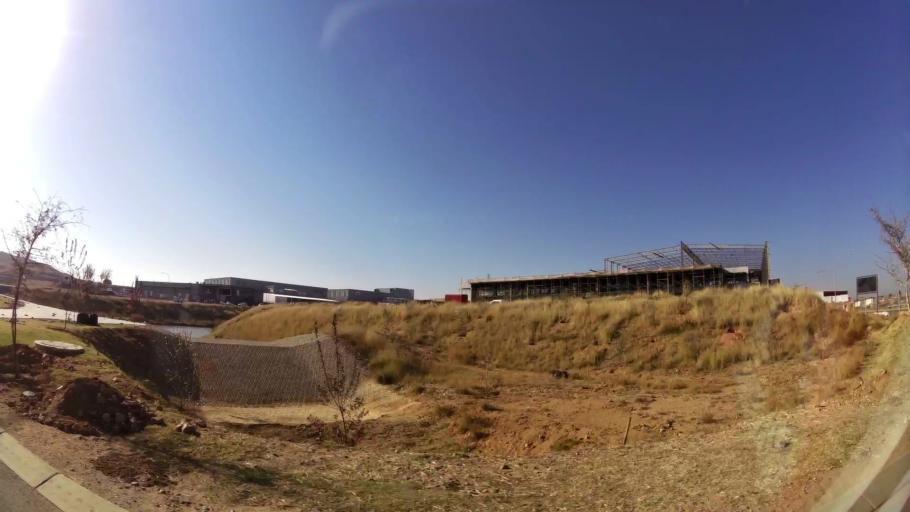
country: ZA
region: Gauteng
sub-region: City of Johannesburg Metropolitan Municipality
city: Modderfontein
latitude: -26.0472
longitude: 28.1635
